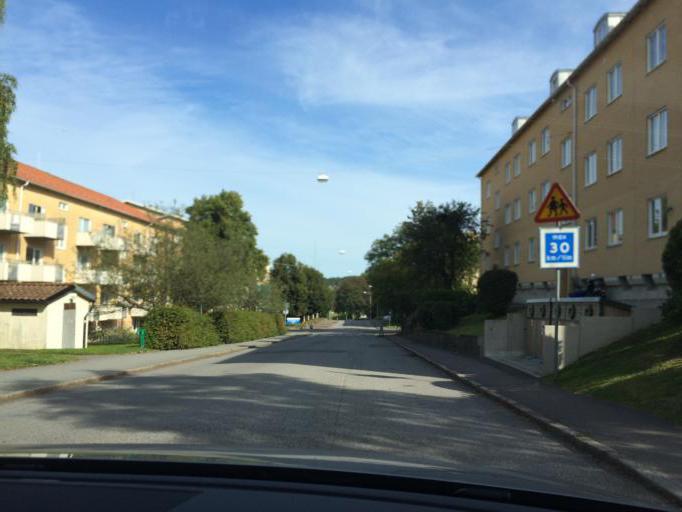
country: SE
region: Vaestra Goetaland
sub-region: Goteborg
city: Goeteborg
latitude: 57.6829
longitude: 11.9895
